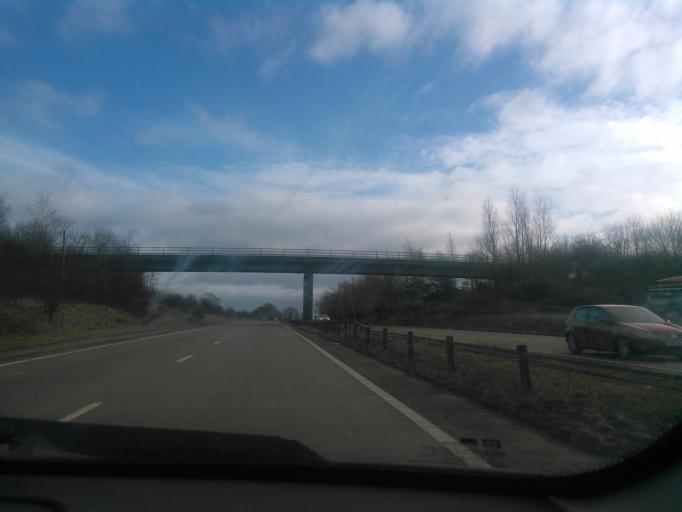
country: GB
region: England
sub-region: Staffordshire
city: Uttoxeter
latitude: 52.9024
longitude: -1.8051
